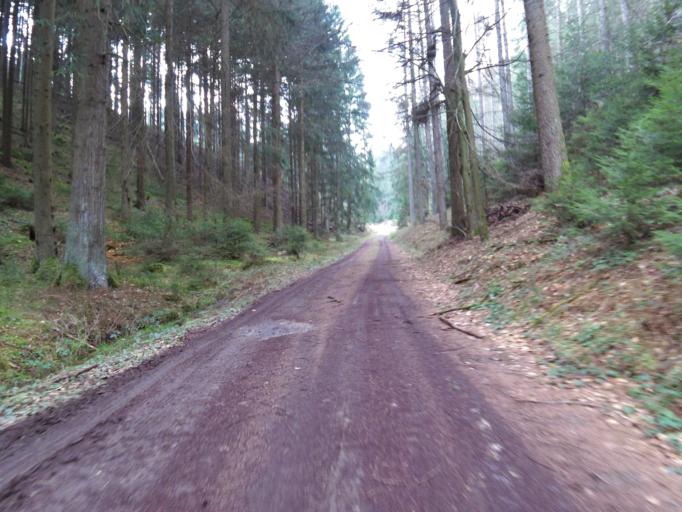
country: DE
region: Rheinland-Pfalz
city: Carlsberg
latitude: 49.4839
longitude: 7.9959
